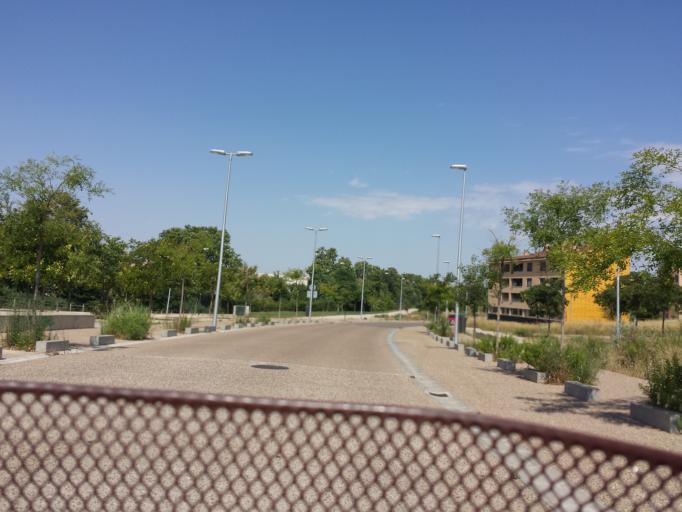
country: ES
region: Aragon
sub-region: Provincia de Zaragoza
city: Montecanal
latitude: 41.6351
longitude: -0.9328
